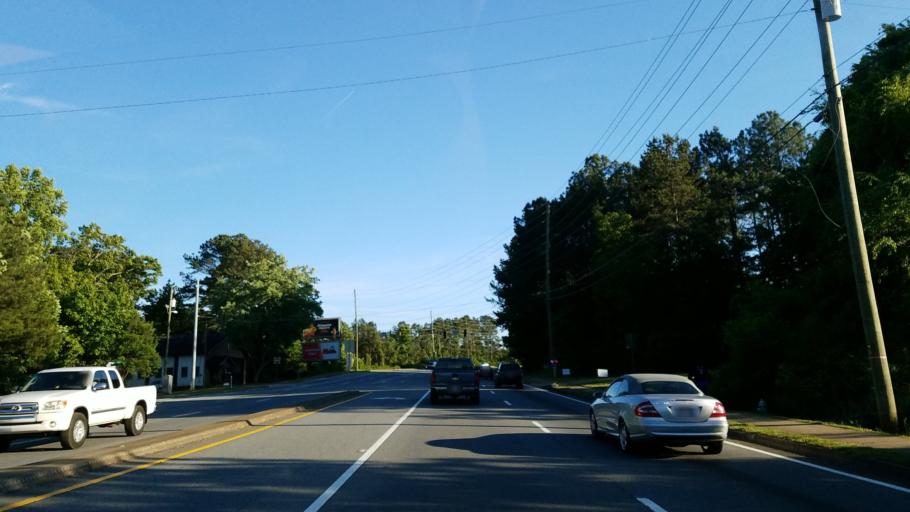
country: US
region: Georgia
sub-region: Cherokee County
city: Woodstock
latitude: 34.1002
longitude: -84.5806
